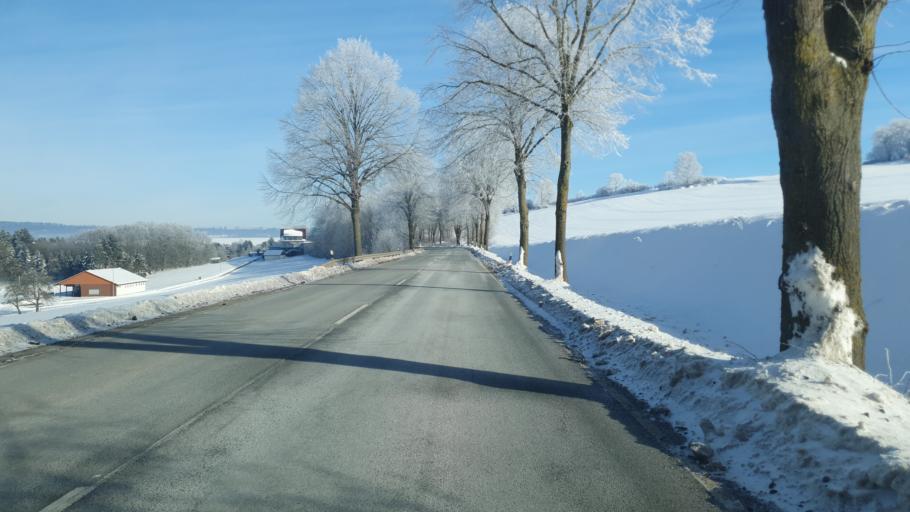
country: DE
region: Lower Saxony
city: Aerzen
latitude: 52.0218
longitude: 9.2235
